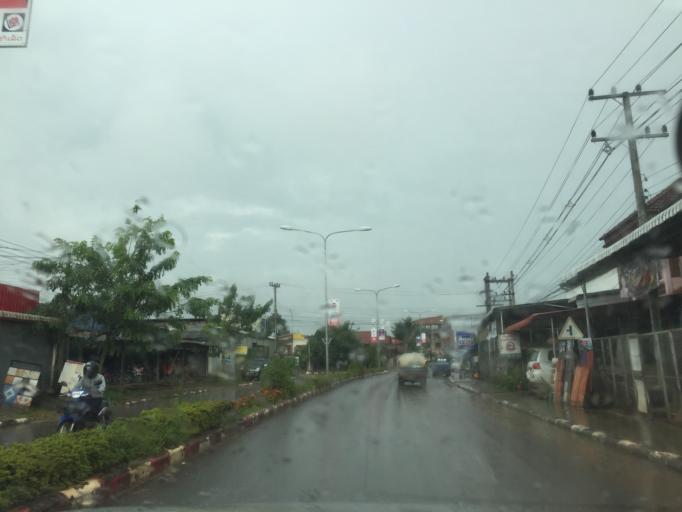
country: LA
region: Attapu
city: Attapu
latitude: 14.8190
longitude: 106.8155
